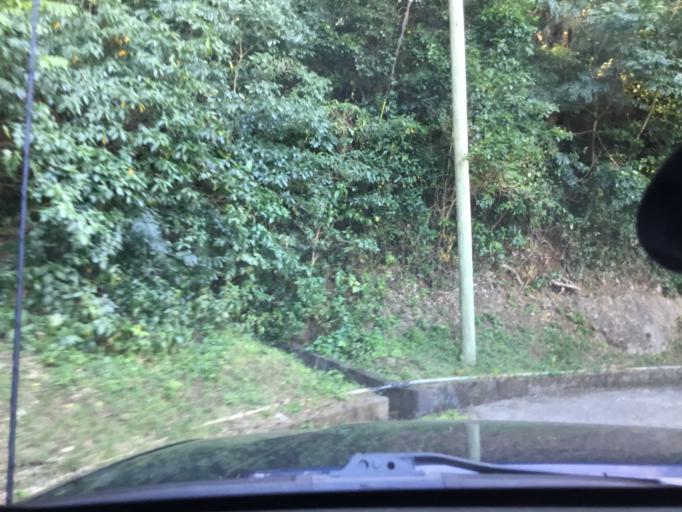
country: VC
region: Charlotte
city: Biabou
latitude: 13.1584
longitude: -61.1687
